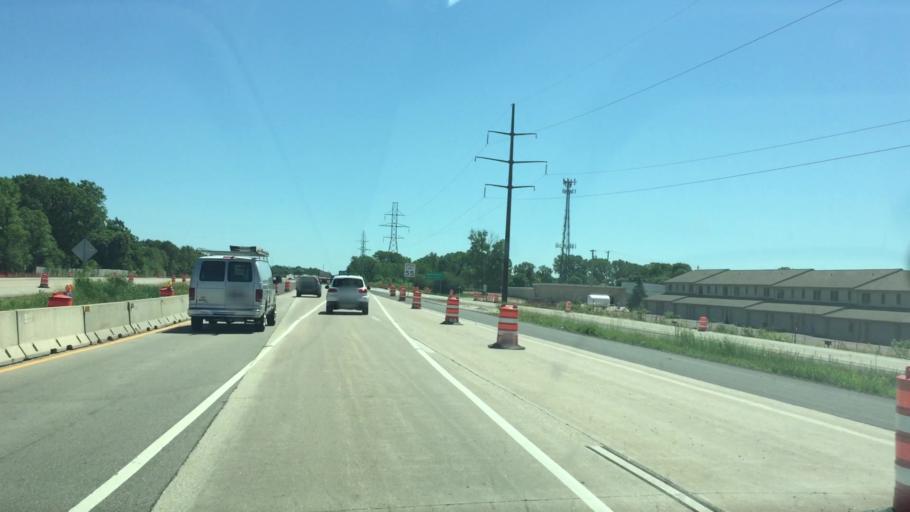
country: US
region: Wisconsin
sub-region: Outagamie County
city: Appleton
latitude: 44.2338
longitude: -88.4210
